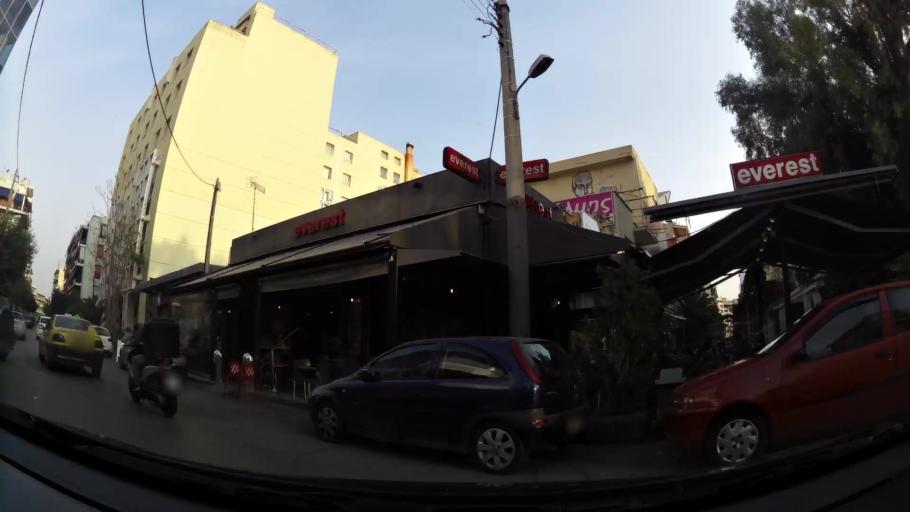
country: GR
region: Attica
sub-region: Nomarchia Athinas
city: Nea Smyrni
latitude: 37.9597
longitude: 23.7183
